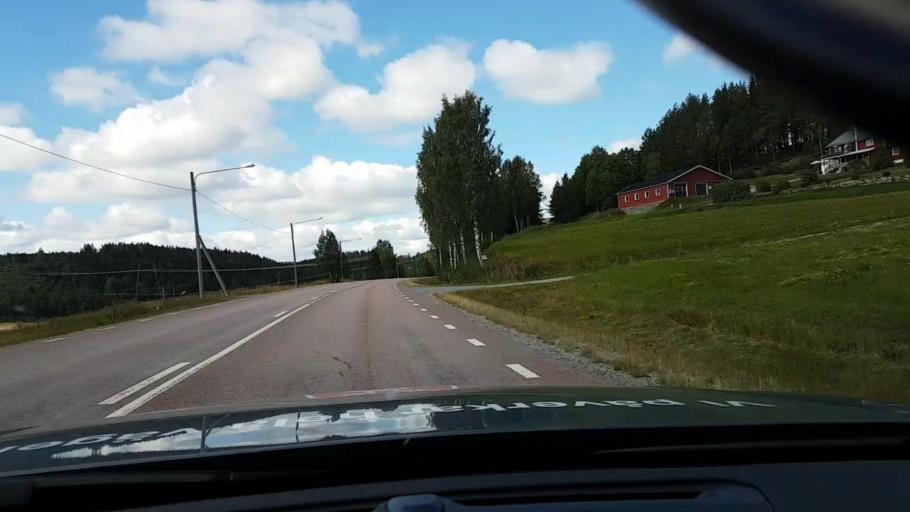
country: SE
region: Vaesternorrland
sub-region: OErnskoeldsviks Kommun
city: Bjasta
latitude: 63.3861
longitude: 18.3754
